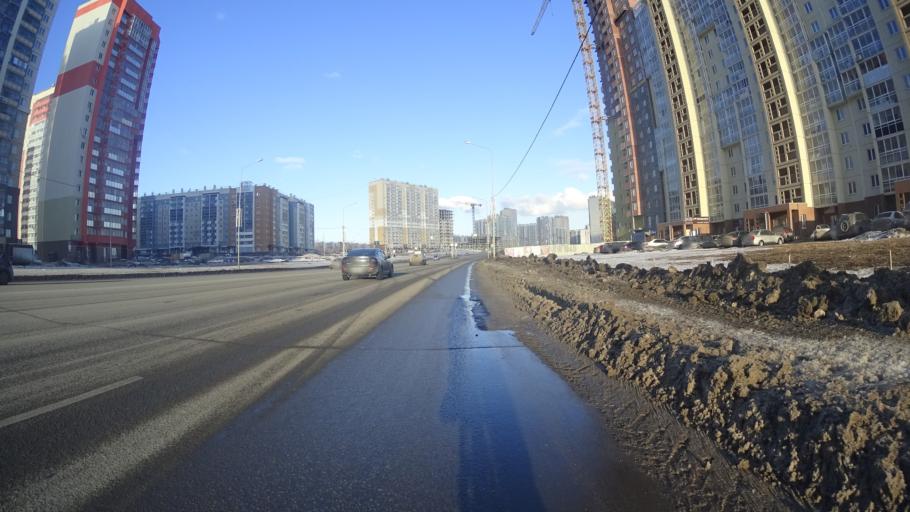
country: RU
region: Chelyabinsk
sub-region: Gorod Chelyabinsk
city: Chelyabinsk
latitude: 55.1727
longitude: 61.3148
